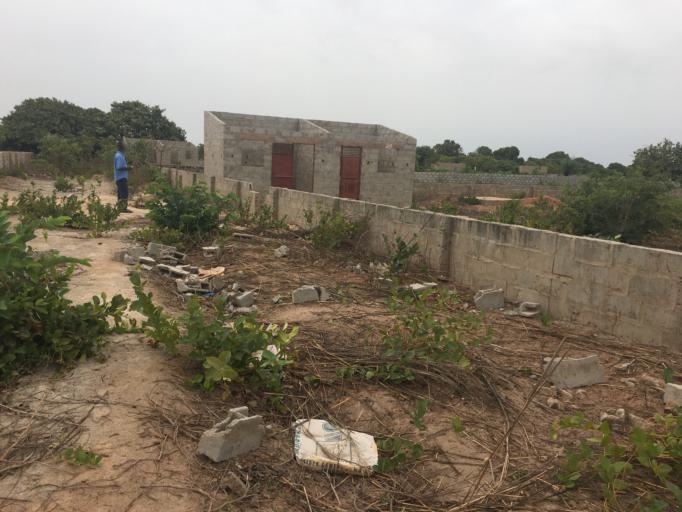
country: GM
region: Western
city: Sukuta
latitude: 13.3140
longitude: -16.7718
